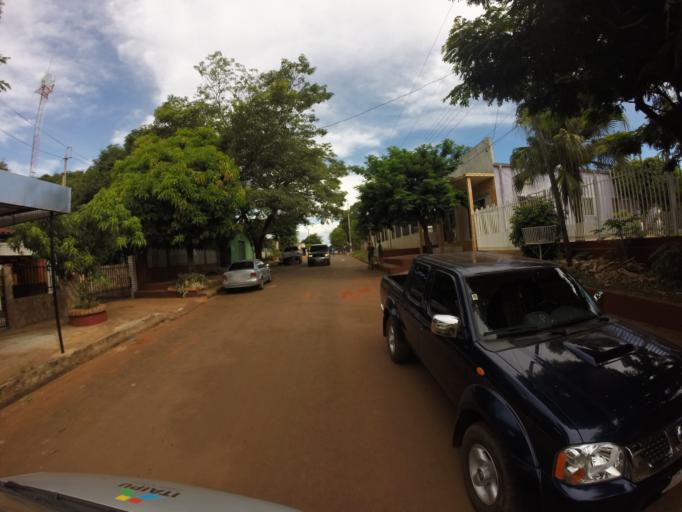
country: PY
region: Alto Parana
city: Ciudad del Este
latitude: -25.4343
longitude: -54.6430
